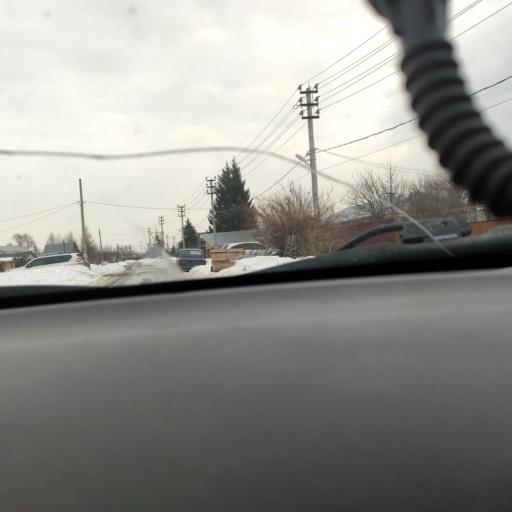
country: RU
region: Tatarstan
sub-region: Gorod Kazan'
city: Kazan
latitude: 55.8991
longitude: 49.1389
